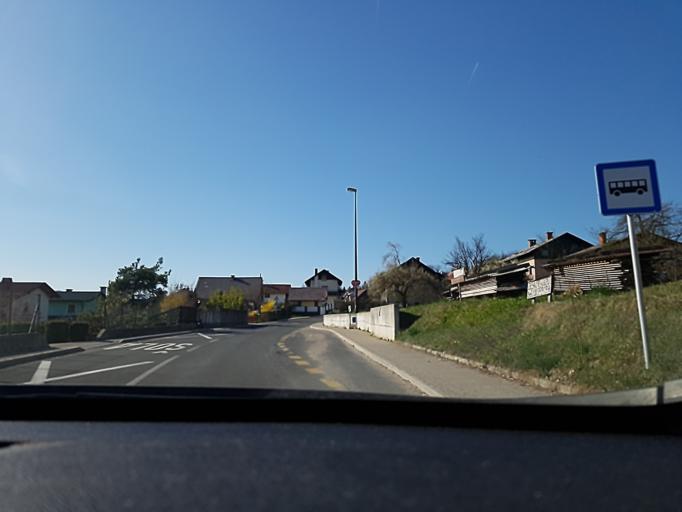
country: SI
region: Medvode
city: Zgornje Pirnice
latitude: 46.1412
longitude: 14.4267
